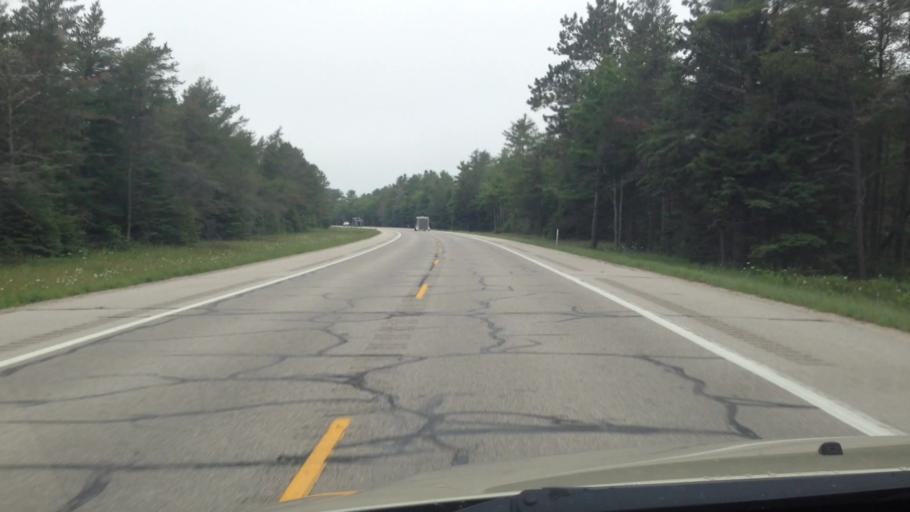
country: US
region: Michigan
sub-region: Luce County
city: Newberry
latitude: 46.0924
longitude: -85.3296
